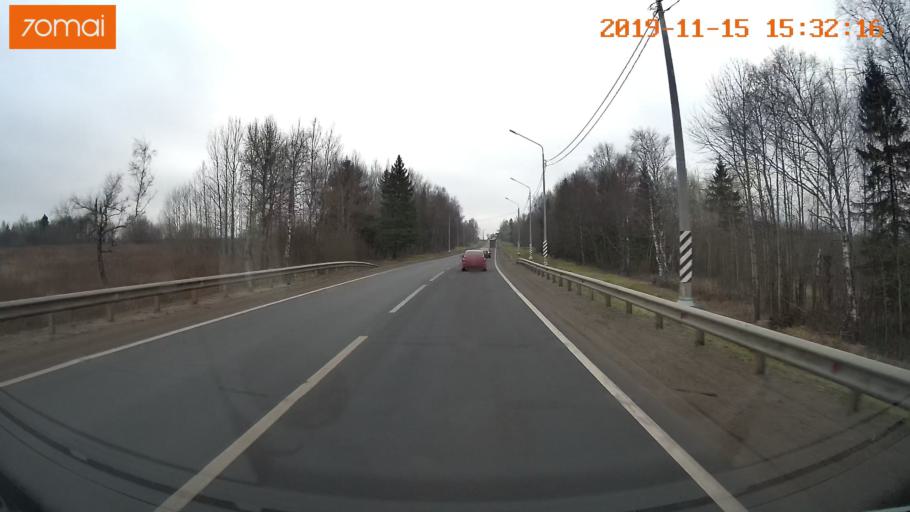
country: RU
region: Jaroslavl
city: Danilov
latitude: 58.0918
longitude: 40.1019
